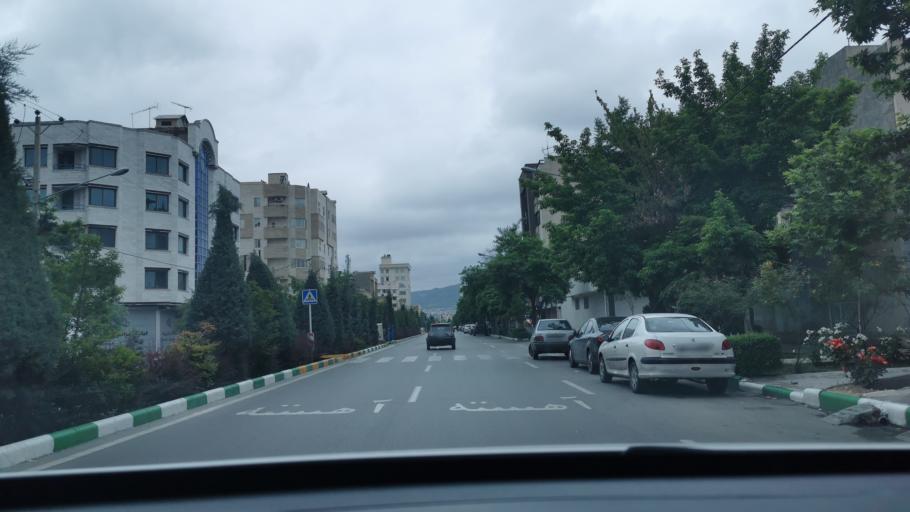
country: IR
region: Razavi Khorasan
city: Mashhad
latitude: 36.3270
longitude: 59.5277
